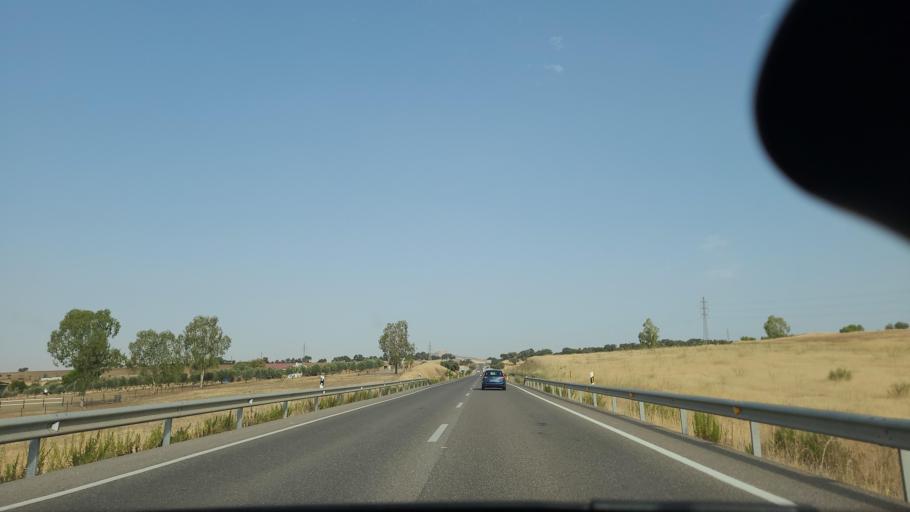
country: ES
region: Andalusia
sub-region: Province of Cordoba
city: Belmez
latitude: 38.2819
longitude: -5.2101
